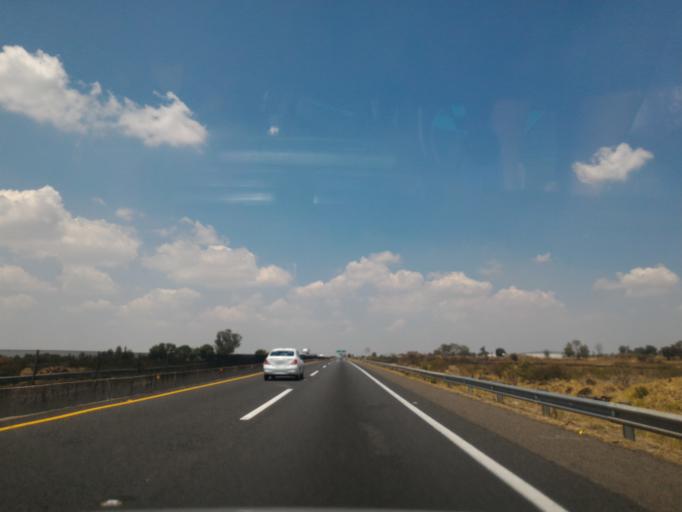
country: MX
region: Jalisco
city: Tepatitlan de Morelos
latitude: 20.8828
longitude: -102.7290
